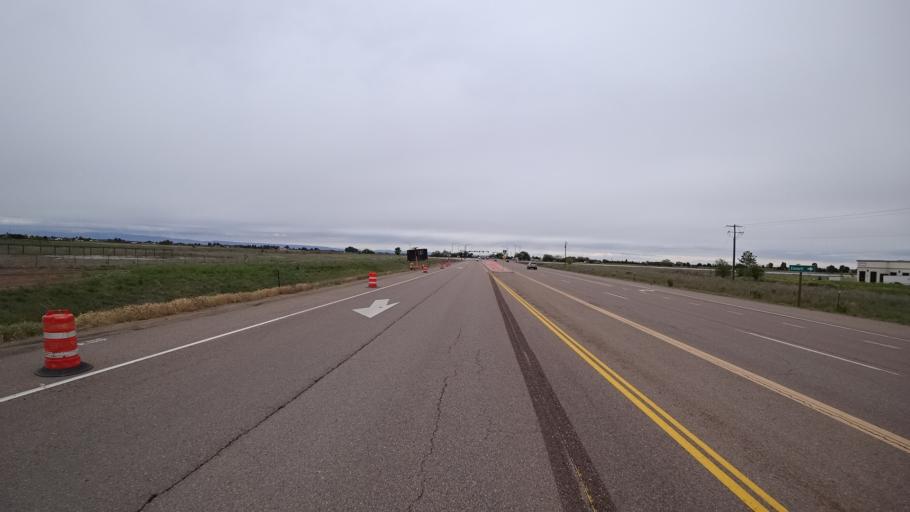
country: US
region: Idaho
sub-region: Ada County
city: Star
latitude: 43.6630
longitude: -116.4688
